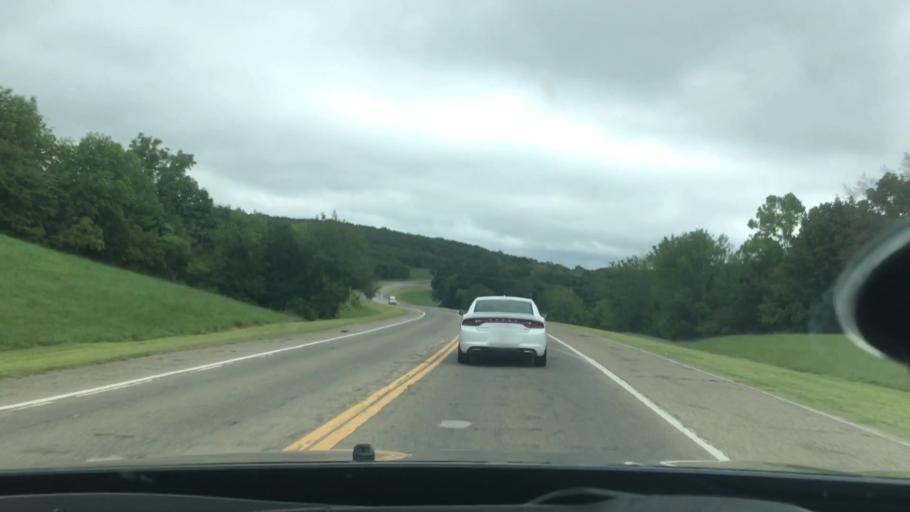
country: US
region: Oklahoma
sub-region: Sequoyah County
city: Vian
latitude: 35.5136
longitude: -94.9697
